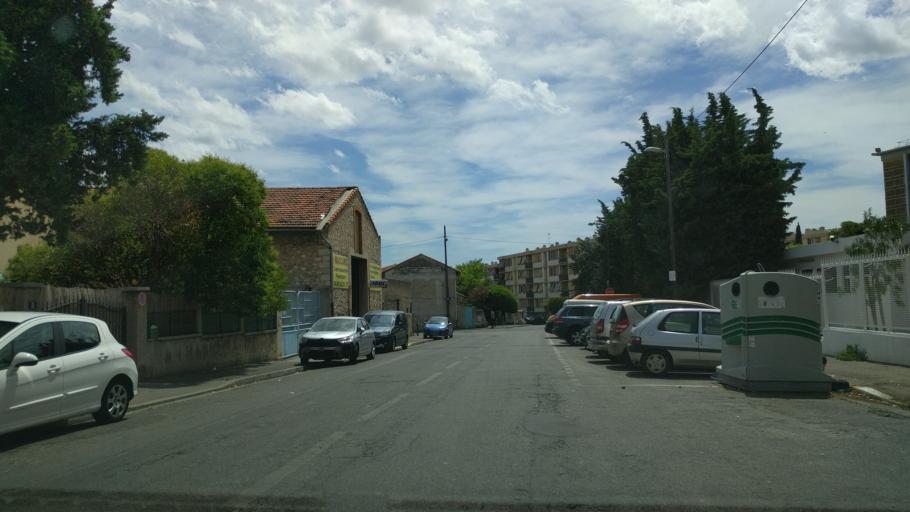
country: FR
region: Provence-Alpes-Cote d'Azur
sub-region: Departement des Bouches-du-Rhone
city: Marseille 13
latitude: 43.3384
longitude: 5.4069
